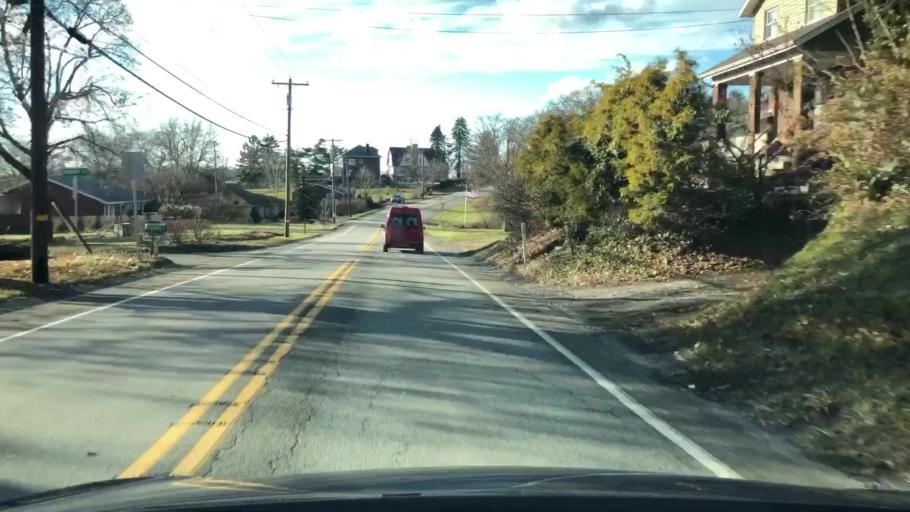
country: US
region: Pennsylvania
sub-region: Butler County
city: Meadowood
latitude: 40.8432
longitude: -79.8757
